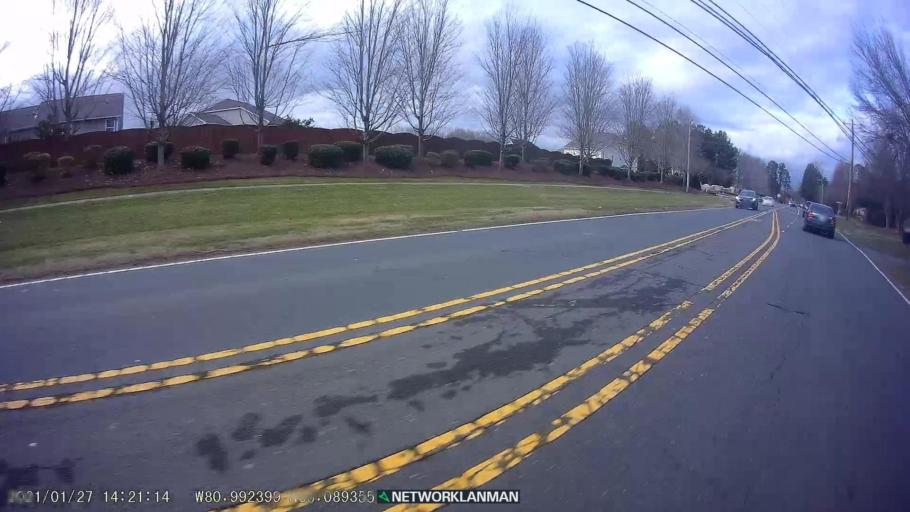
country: US
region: South Carolina
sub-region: York County
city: Lake Wylie
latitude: 35.0896
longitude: -80.9926
